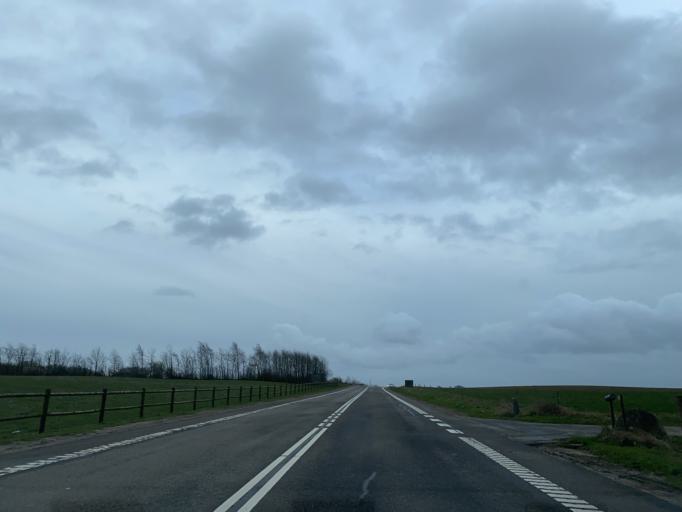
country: DK
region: Central Jutland
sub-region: Viborg Kommune
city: Bjerringbro
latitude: 56.2970
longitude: 9.6006
